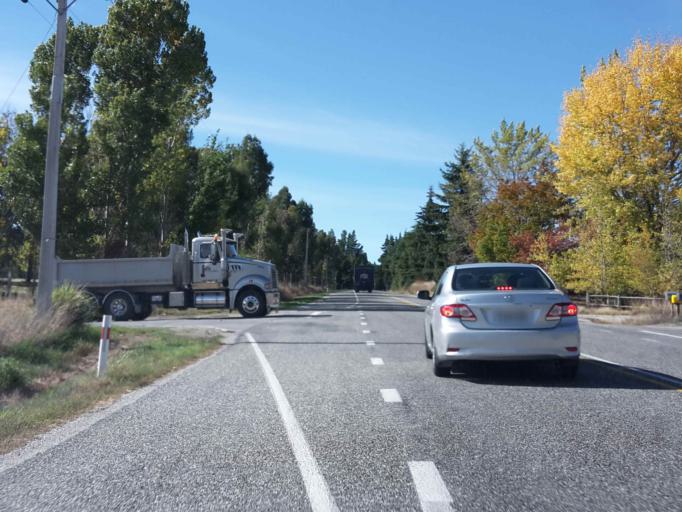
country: NZ
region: Otago
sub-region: Queenstown-Lakes District
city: Wanaka
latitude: -44.7007
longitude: 169.1874
